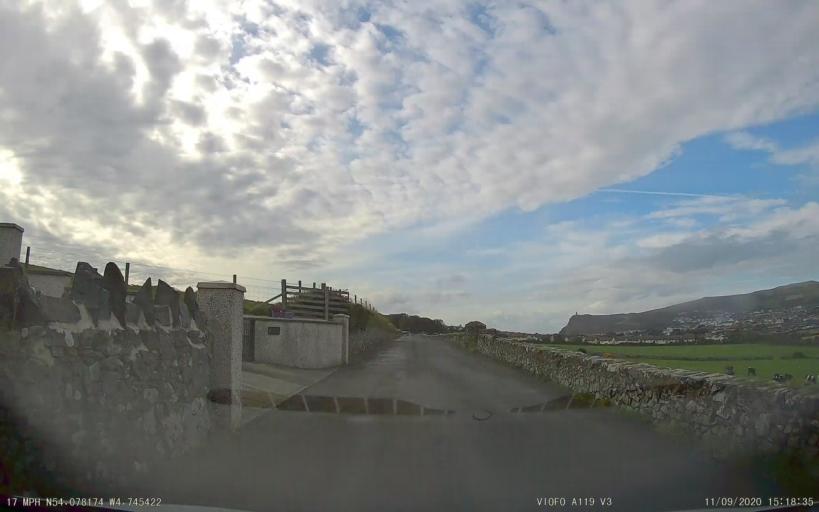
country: IM
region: Port Erin
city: Port Erin
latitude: 54.0782
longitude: -4.7452
